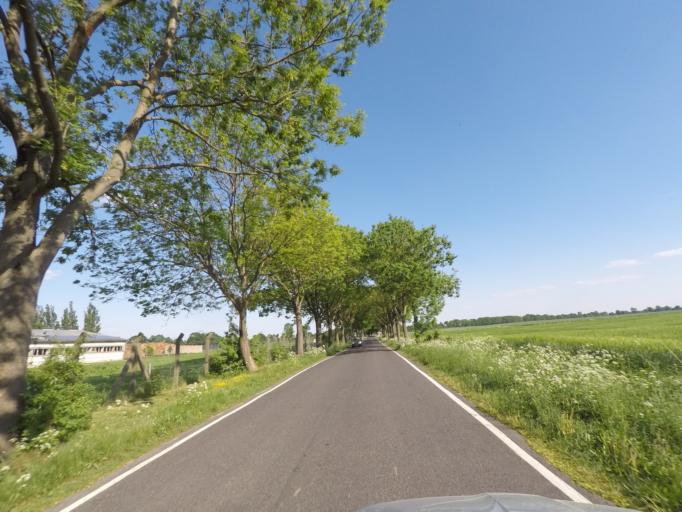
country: DE
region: Brandenburg
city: Hohenfinow
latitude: 52.7172
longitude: 13.9055
